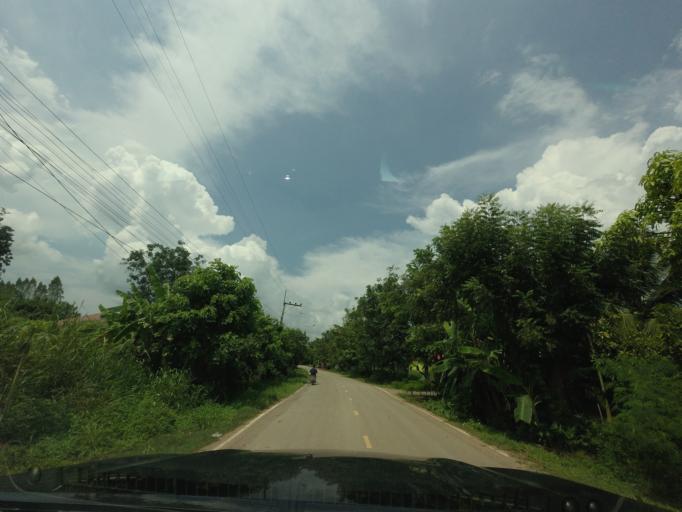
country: TH
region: Khon Kaen
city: Wiang Kao
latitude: 16.6808
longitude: 102.2834
